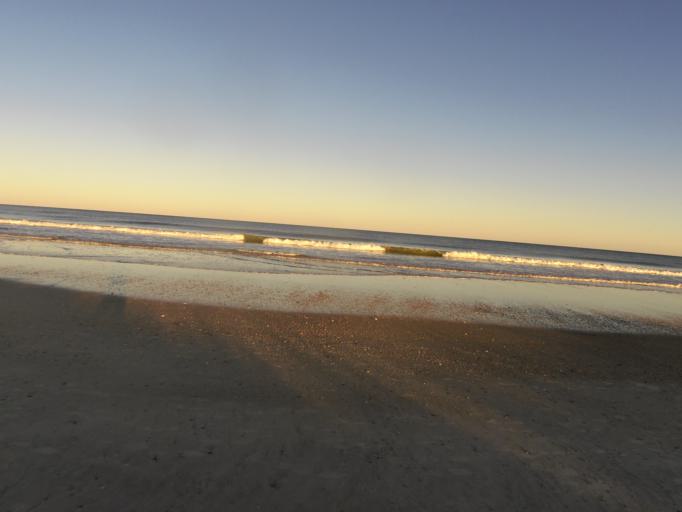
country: US
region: Florida
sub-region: Duval County
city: Atlantic Beach
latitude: 30.4622
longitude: -81.4115
